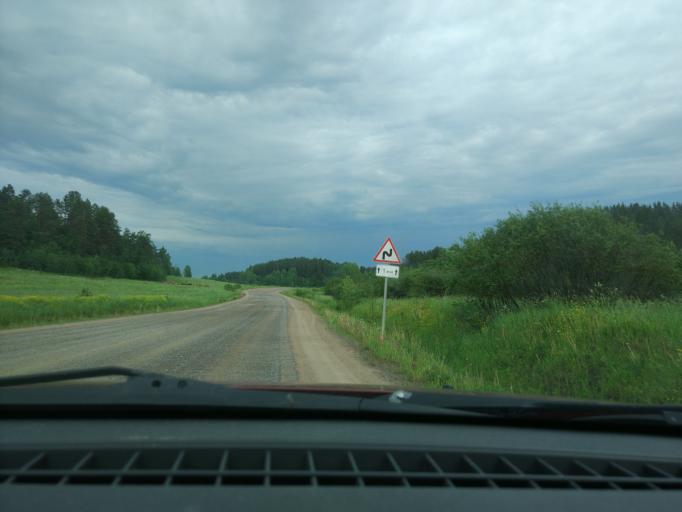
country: RU
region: Leningrad
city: Kuznechnoye
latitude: 61.2778
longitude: 29.8490
